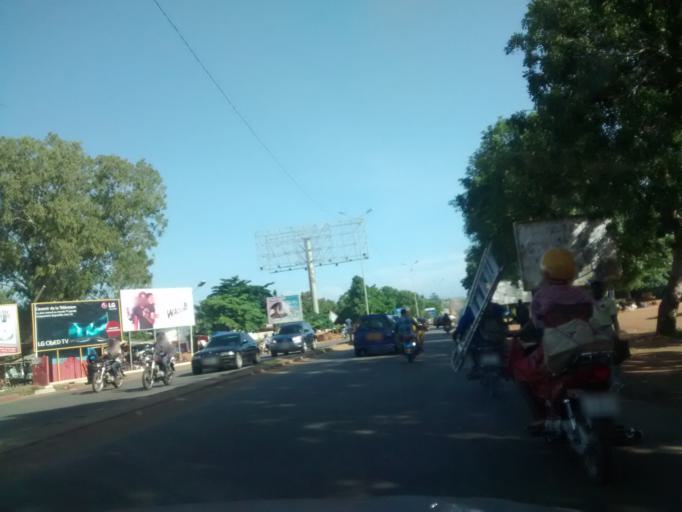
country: TG
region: Maritime
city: Lome
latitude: 6.1657
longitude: 1.2020
